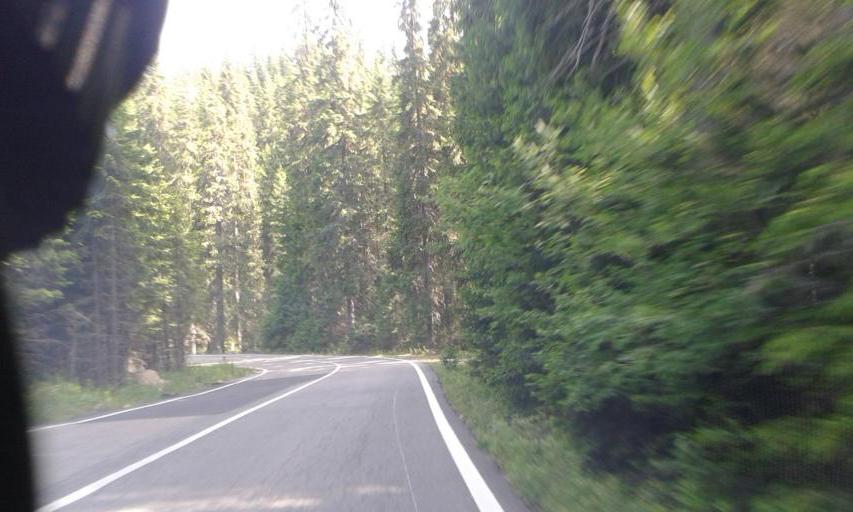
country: RO
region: Hunedoara
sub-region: Oras Petrila
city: Petrila
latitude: 45.5208
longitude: 23.6493
